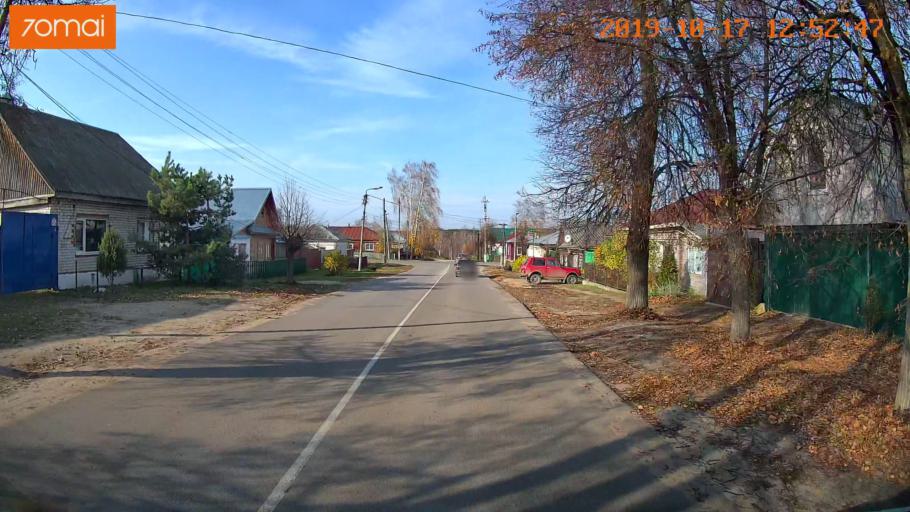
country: RU
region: Rjazan
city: Kasimov
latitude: 54.9440
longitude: 41.3870
